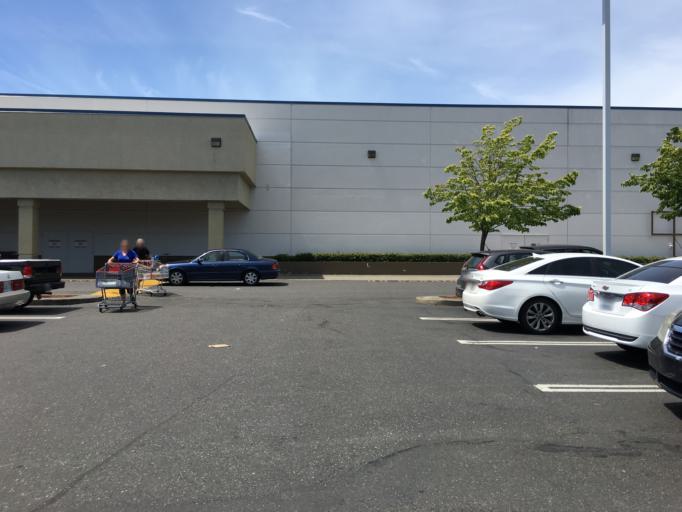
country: US
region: Washington
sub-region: Whatcom County
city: Bellingham
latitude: 48.7984
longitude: -122.4882
